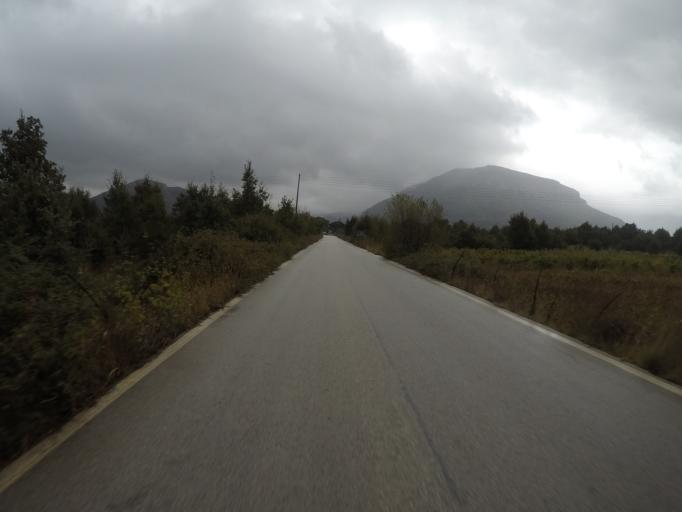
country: GR
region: Peloponnese
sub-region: Nomos Arkadias
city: Tripoli
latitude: 37.5829
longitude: 22.4222
